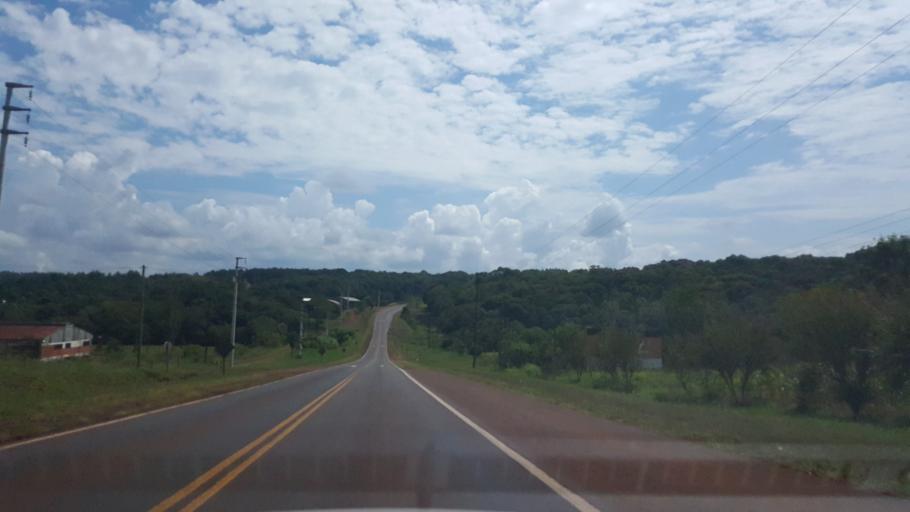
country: AR
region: Misiones
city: Capiovi
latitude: -26.8639
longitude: -55.0451
